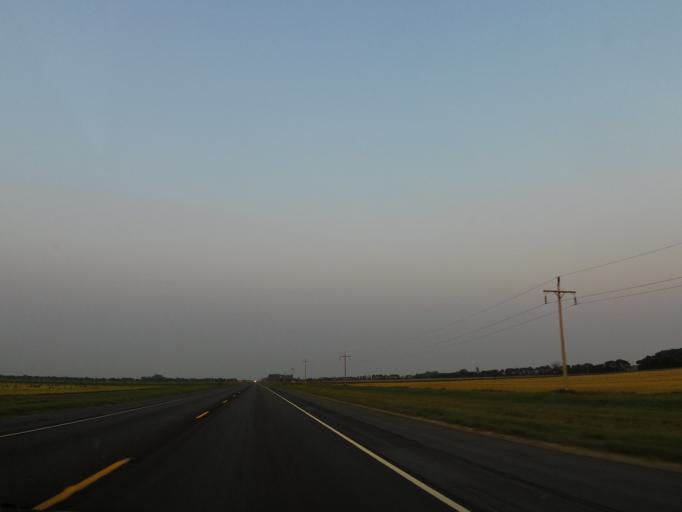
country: US
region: North Dakota
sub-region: Walsh County
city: Grafton
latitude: 48.4127
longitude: -97.5618
